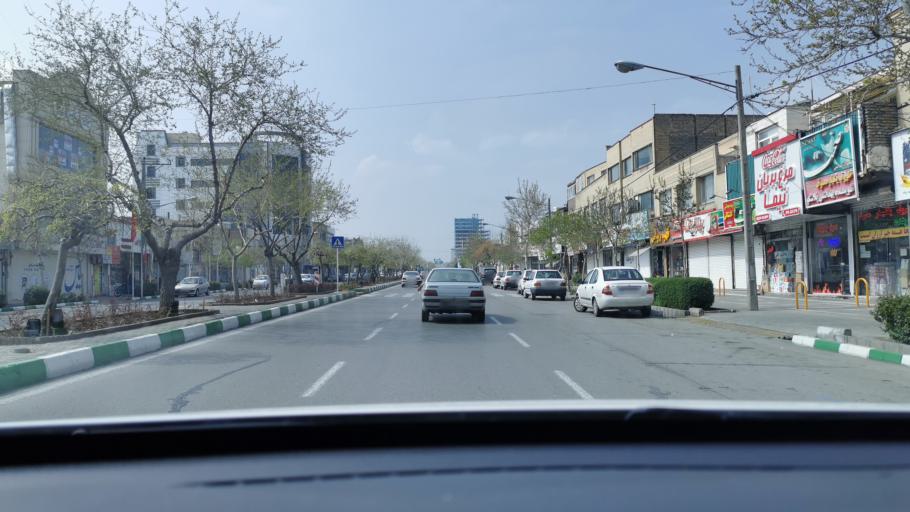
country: IR
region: Razavi Khorasan
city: Mashhad
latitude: 36.3301
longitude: 59.5230
